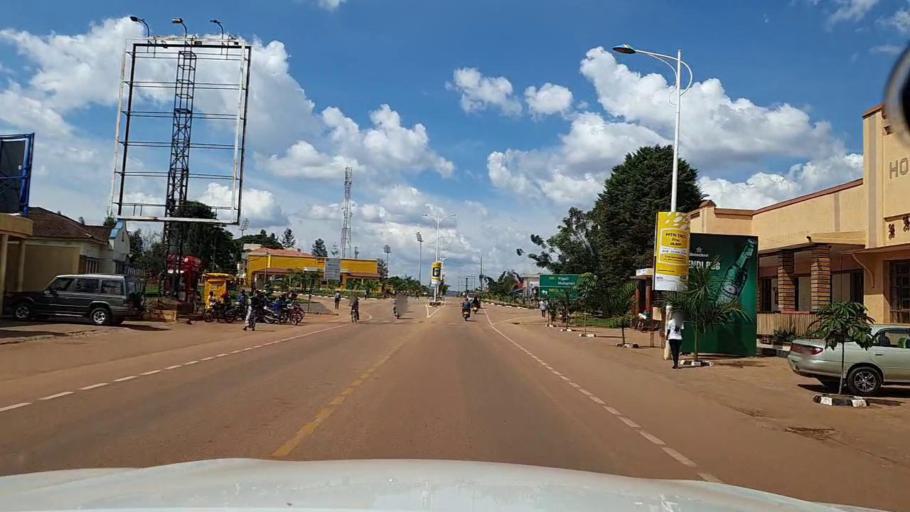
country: RW
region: Southern Province
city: Butare
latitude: -2.6013
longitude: 29.7418
